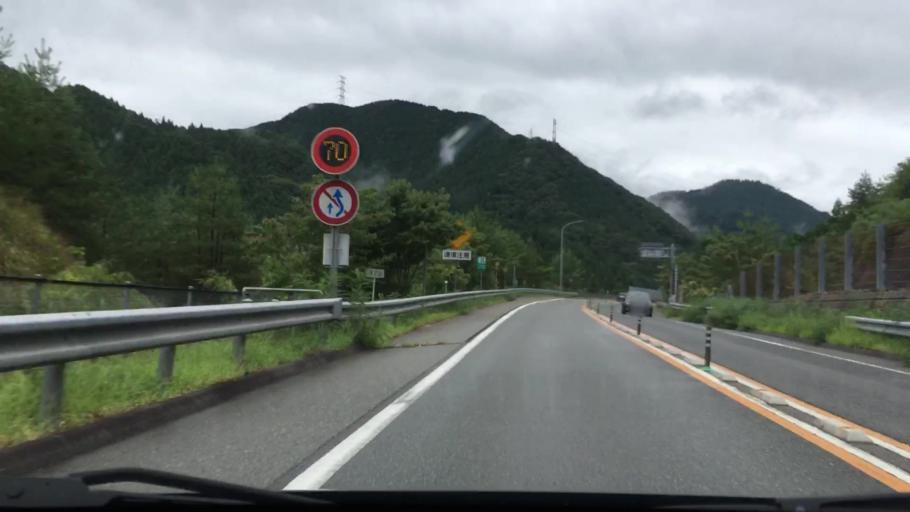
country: JP
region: Hyogo
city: Nishiwaki
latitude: 35.1944
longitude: 134.7900
